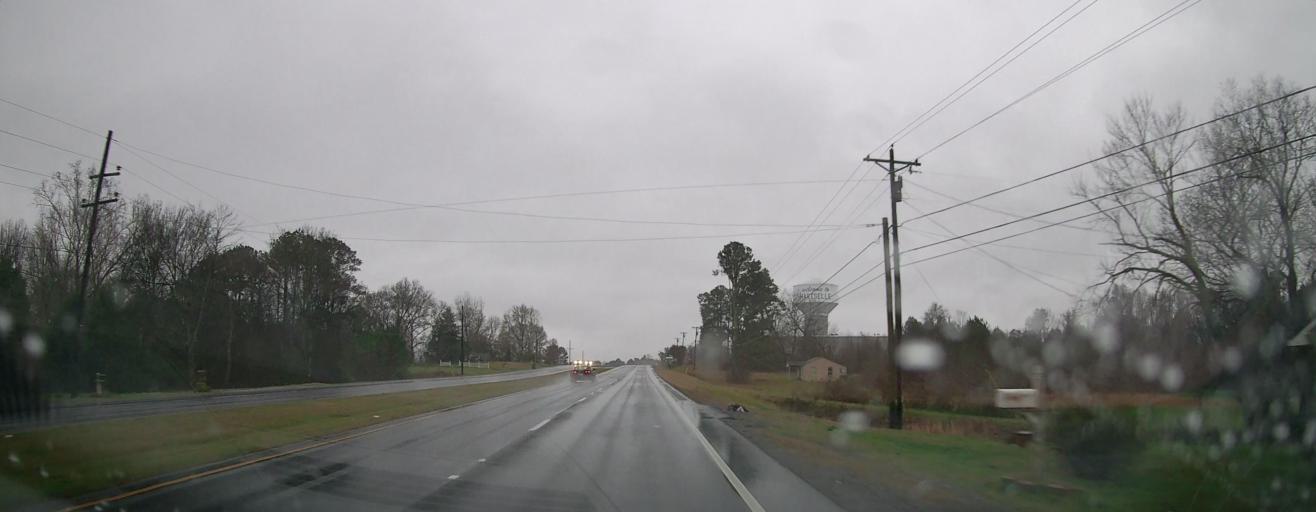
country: US
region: Alabama
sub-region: Morgan County
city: Hartselle
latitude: 34.4790
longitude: -86.9614
